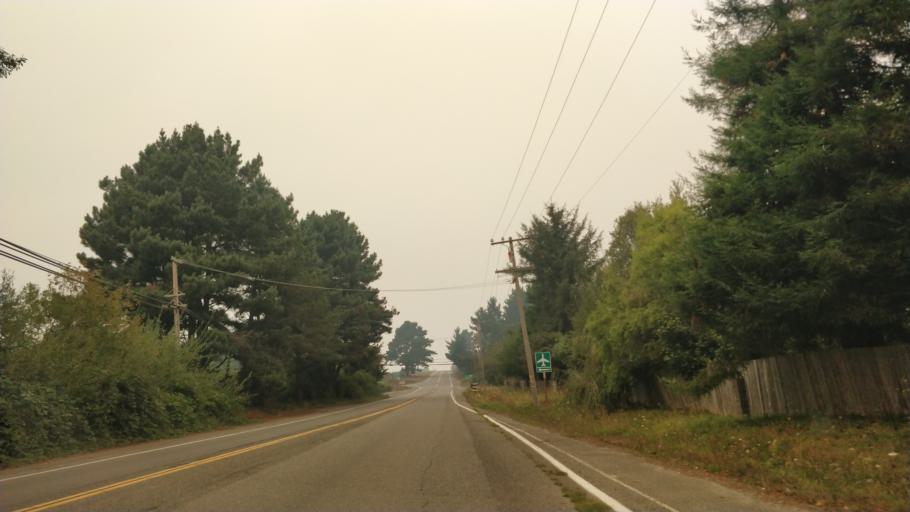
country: US
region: California
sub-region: Humboldt County
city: McKinleyville
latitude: 40.9619
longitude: -124.1008
